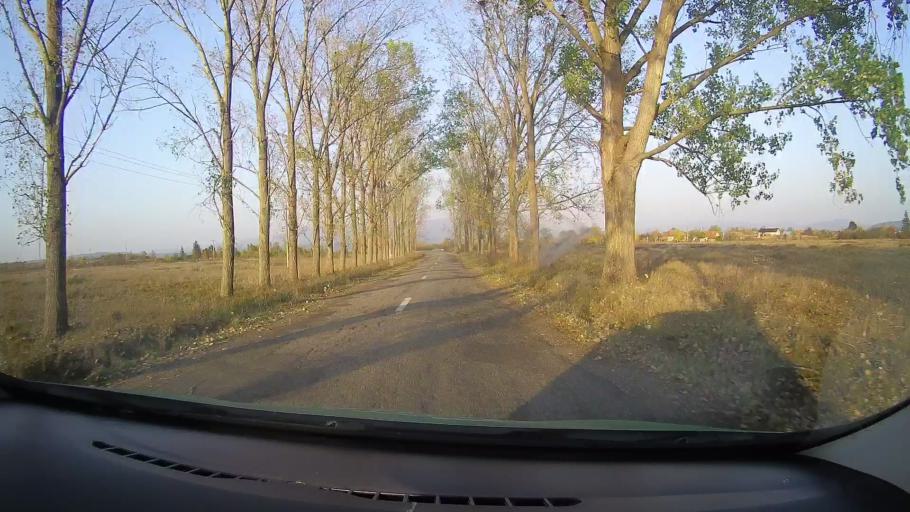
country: RO
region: Arad
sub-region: Comuna Barsa
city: Barsa
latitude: 46.3850
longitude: 22.0643
